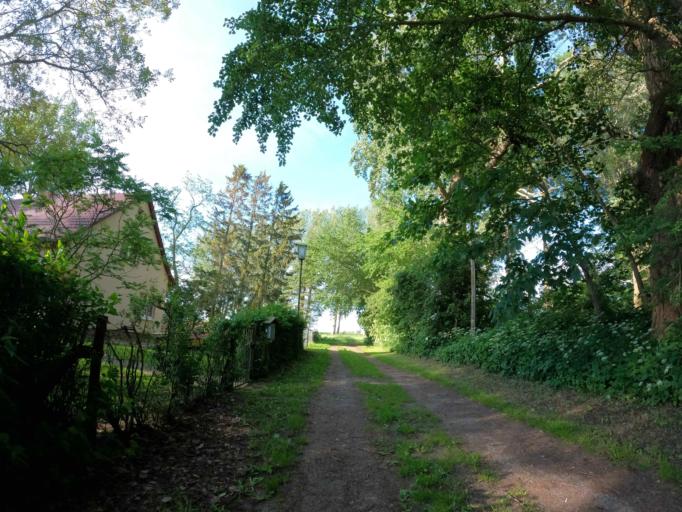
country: DE
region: Mecklenburg-Vorpommern
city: Altenpleen
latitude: 54.3329
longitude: 12.9681
